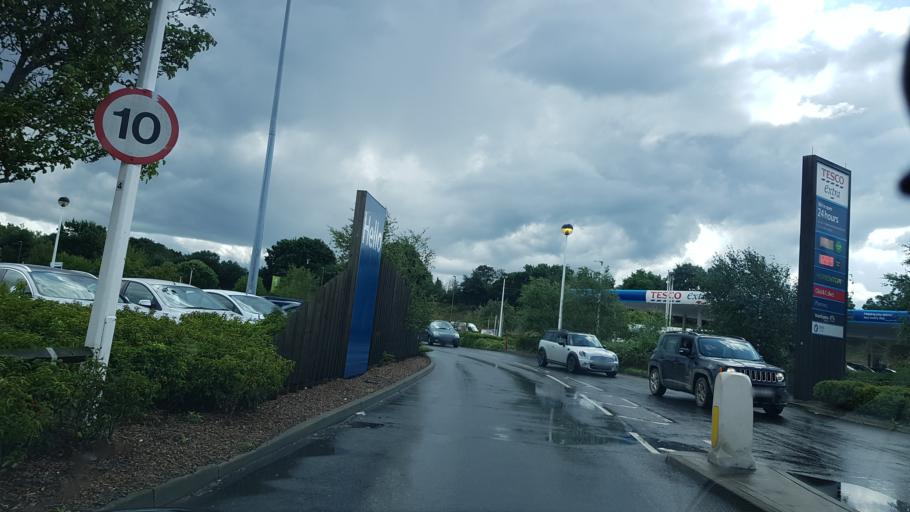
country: GB
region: England
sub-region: Surrey
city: Byfleet
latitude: 51.3442
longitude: -0.4753
